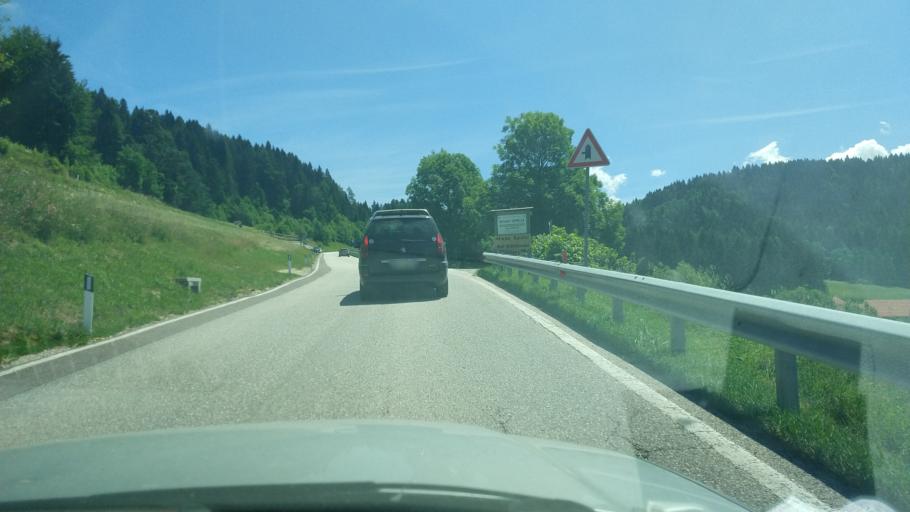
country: IT
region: Trentino-Alto Adige
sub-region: Provincia di Trento
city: Folgaria
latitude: 45.9194
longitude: 11.1962
